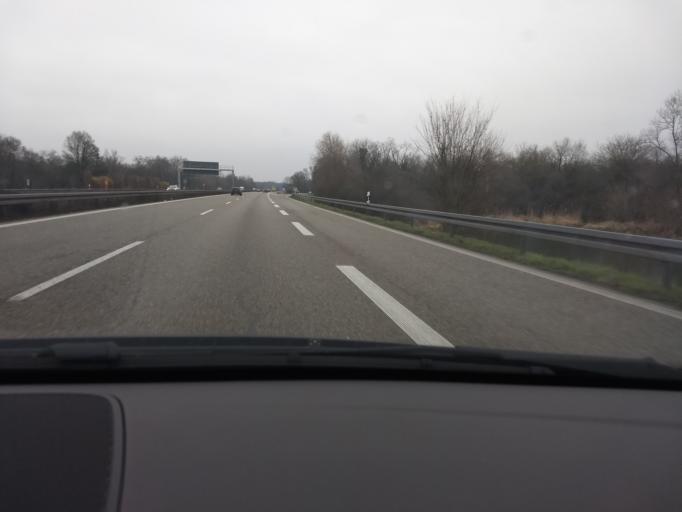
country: FR
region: Alsace
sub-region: Departement du Haut-Rhin
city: Ottmarsheim
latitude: 47.7875
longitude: 7.5375
